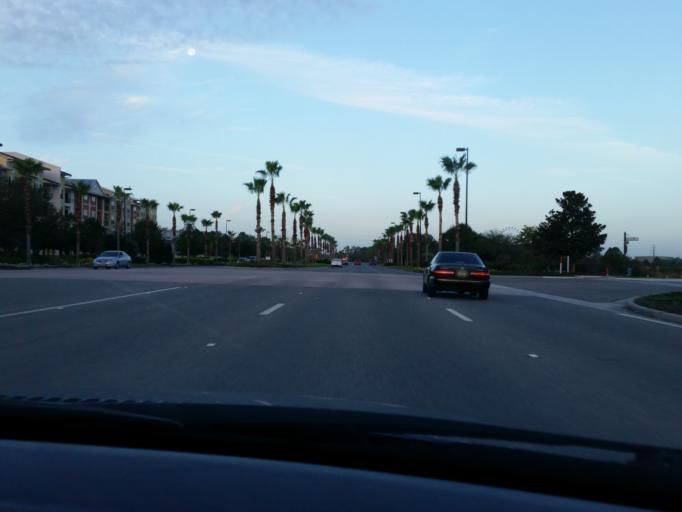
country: US
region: Florida
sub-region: Orange County
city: Williamsburg
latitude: 28.4306
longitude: -81.4473
